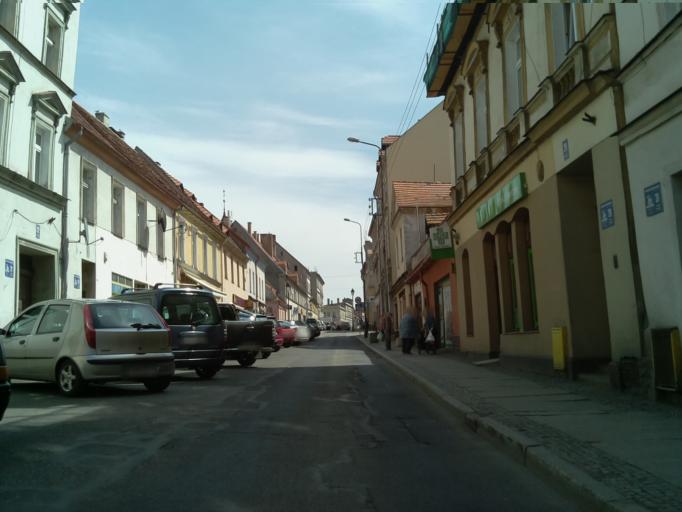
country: PL
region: Lower Silesian Voivodeship
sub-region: Powiat swidnicki
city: Swiebodzice
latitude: 50.8601
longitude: 16.3167
